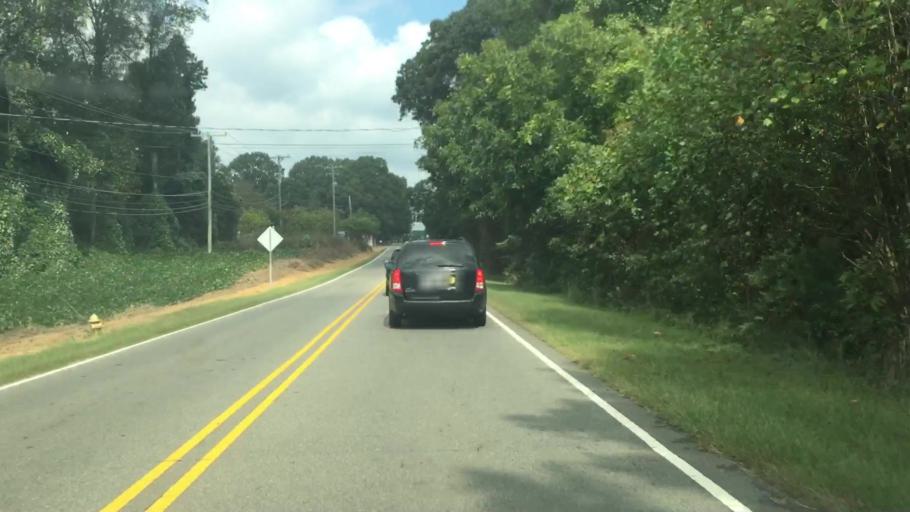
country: US
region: North Carolina
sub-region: Gaston County
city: Davidson
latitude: 35.5501
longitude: -80.8448
